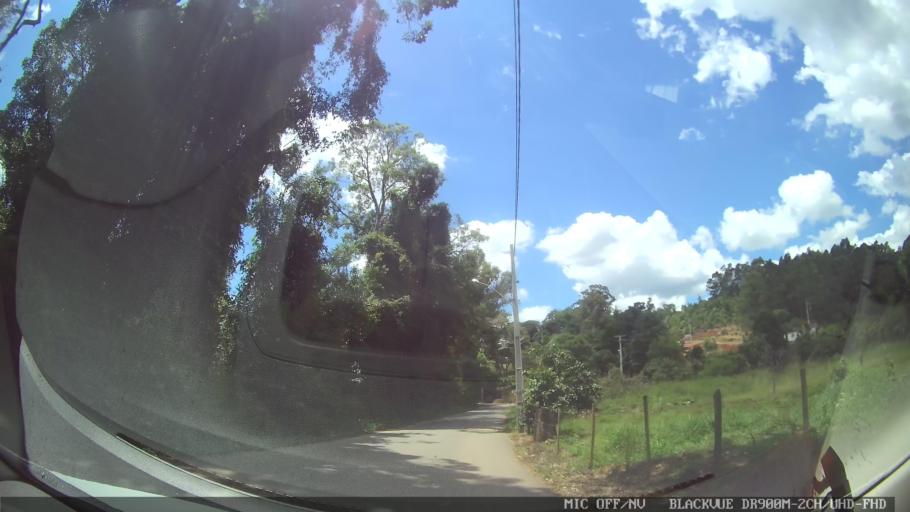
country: BR
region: Minas Gerais
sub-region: Extrema
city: Extrema
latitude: -22.8569
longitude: -46.2799
